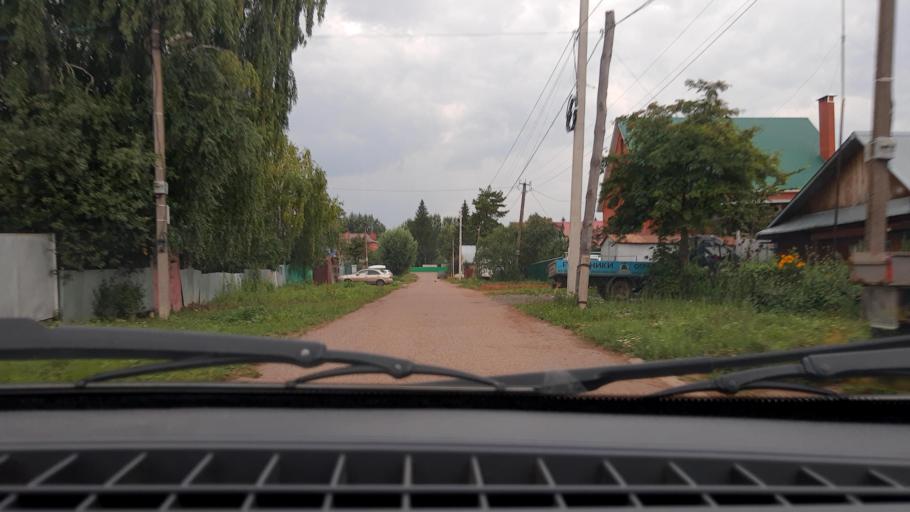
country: RU
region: Bashkortostan
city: Mikhaylovka
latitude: 54.8060
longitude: 55.8088
